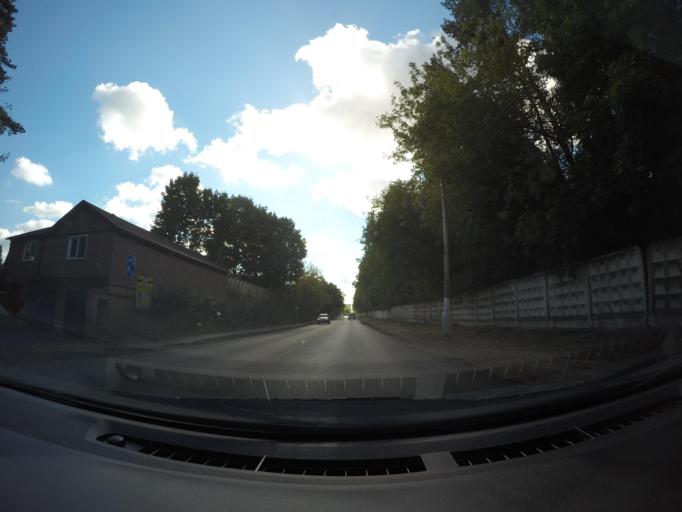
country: RU
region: Moskovskaya
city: Kratovo
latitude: 55.5879
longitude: 38.1916
